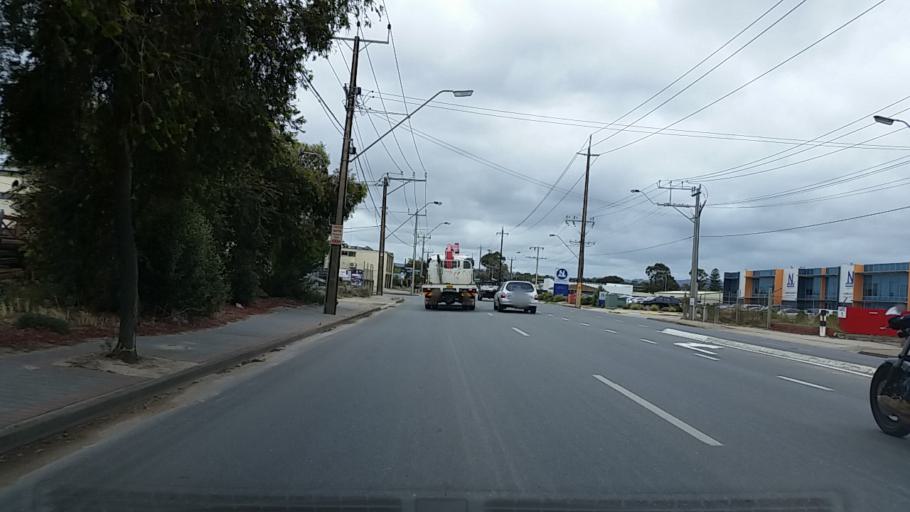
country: AU
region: South Australia
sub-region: Port Adelaide Enfield
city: Blair Athol
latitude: -34.8486
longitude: 138.5882
